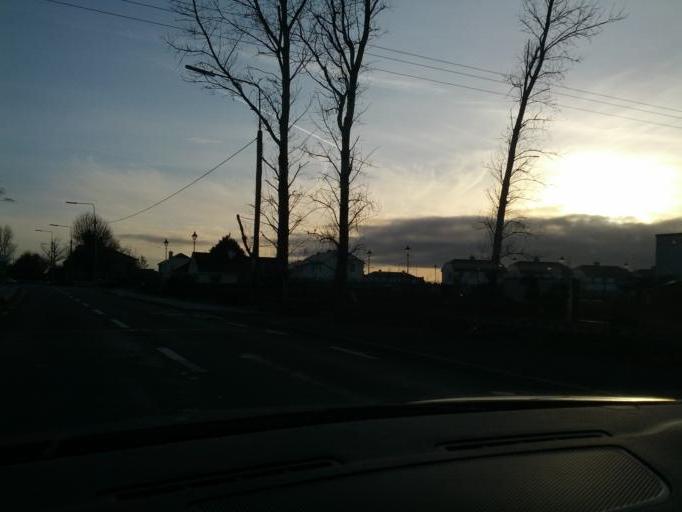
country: IE
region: Connaught
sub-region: Sligo
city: Tobercurry
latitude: 54.0583
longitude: -8.7223
